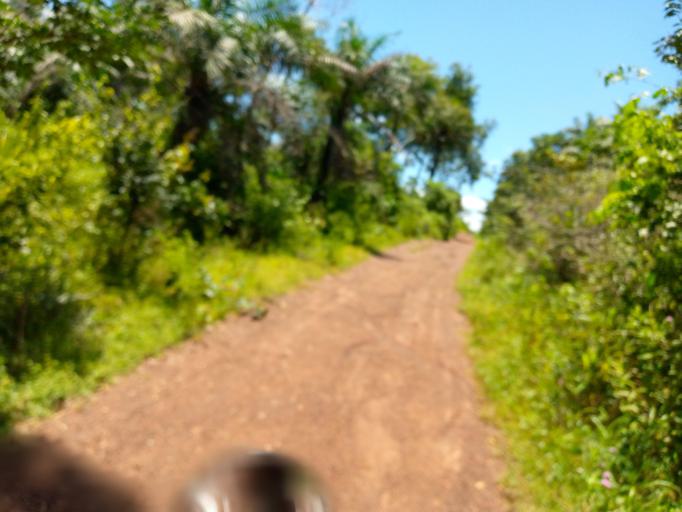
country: SL
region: Northern Province
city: Binkolo
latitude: 9.1173
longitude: -12.1342
